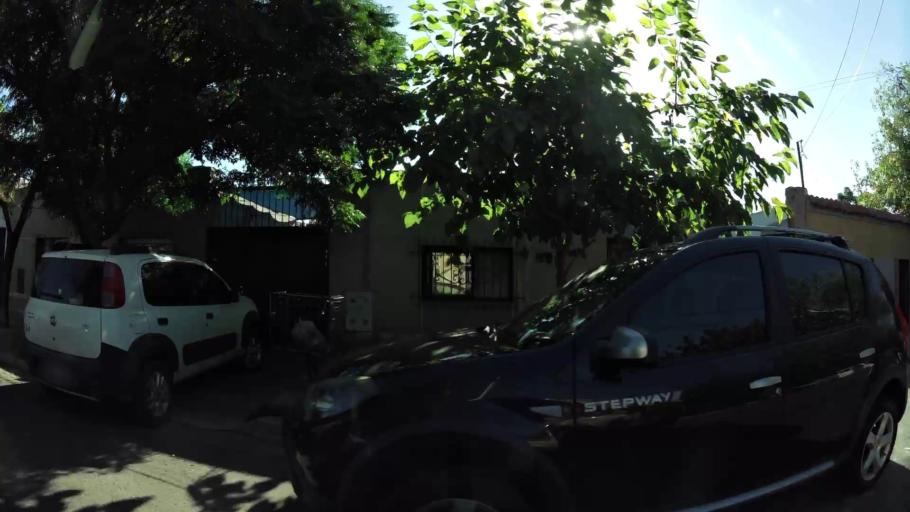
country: AR
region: Mendoza
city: Mendoza
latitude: -32.8992
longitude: -68.8328
